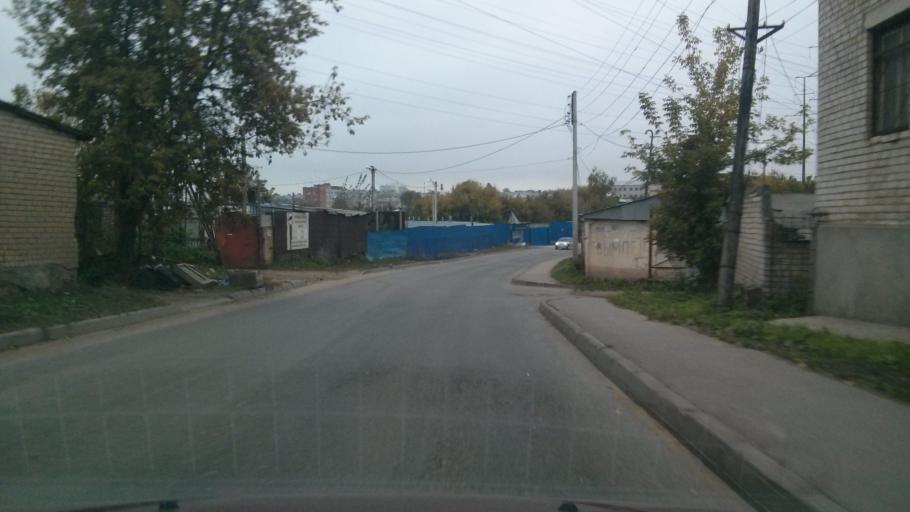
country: RU
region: Nizjnij Novgorod
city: Nizhniy Novgorod
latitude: 56.3082
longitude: 44.0097
